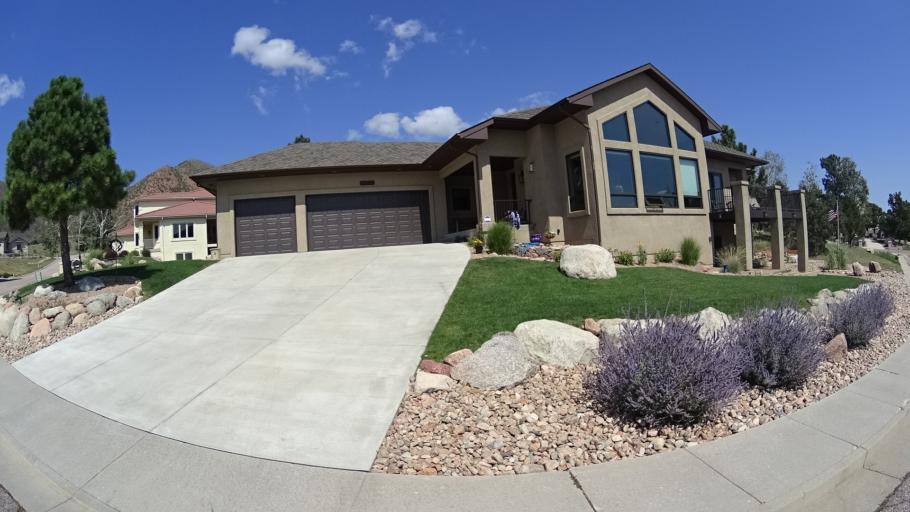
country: US
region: Colorado
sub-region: El Paso County
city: Manitou Springs
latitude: 38.9187
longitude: -104.8802
